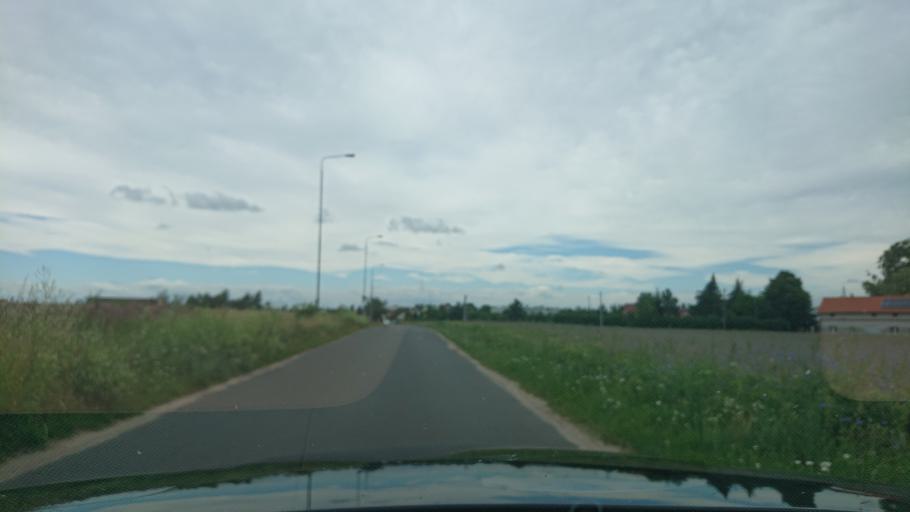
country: PL
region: Greater Poland Voivodeship
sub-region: Powiat gnieznienski
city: Gniezno
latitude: 52.5092
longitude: 17.6076
